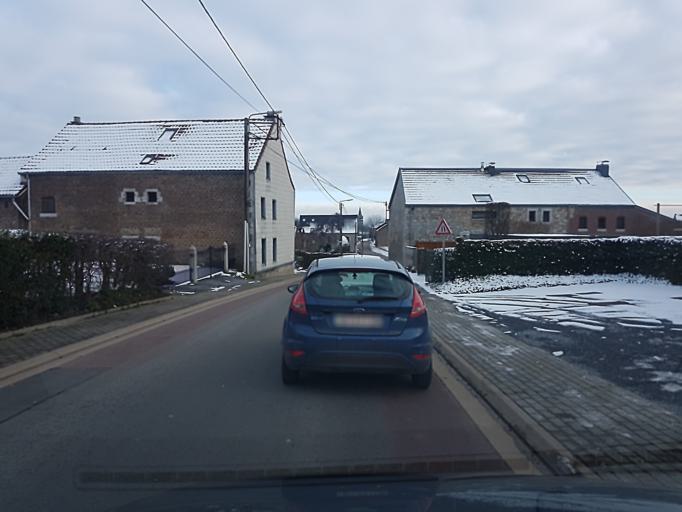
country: BE
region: Wallonia
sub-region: Province de Liege
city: Soumagne
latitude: 50.6068
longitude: 5.7751
